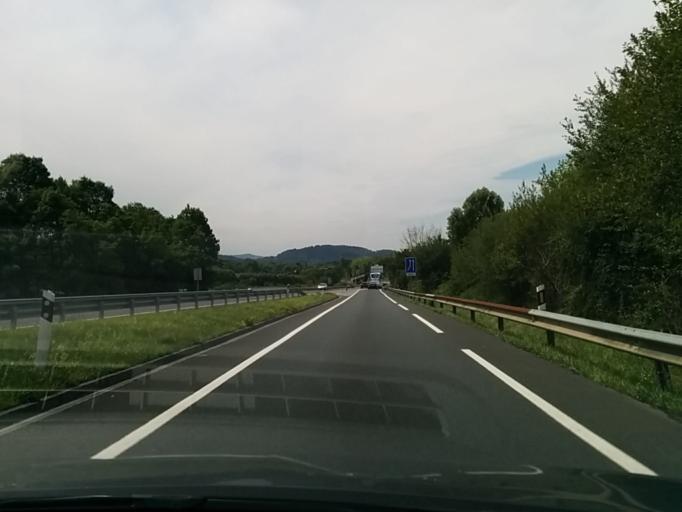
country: ES
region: Basque Country
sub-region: Provincia de Guipuzcoa
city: Irun
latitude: 43.3466
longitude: -1.8133
